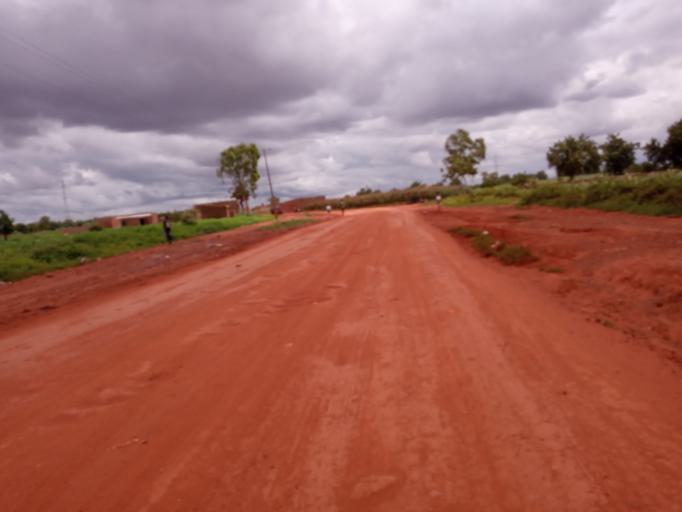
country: ML
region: Bamako
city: Bamako
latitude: 12.5439
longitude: -7.9941
